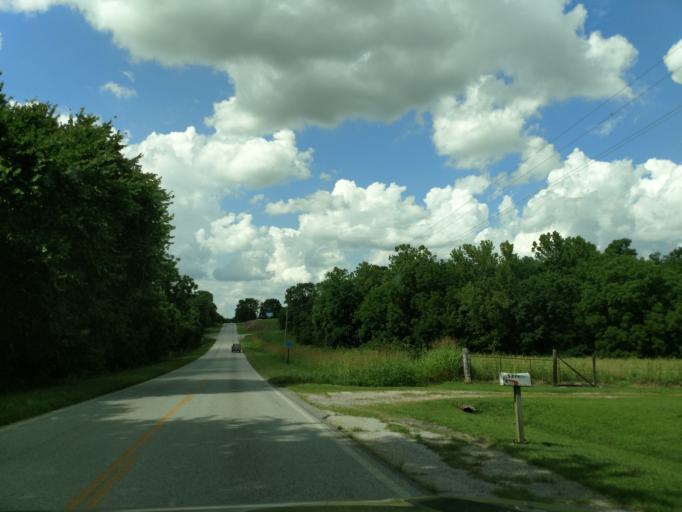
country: US
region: Arkansas
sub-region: Carroll County
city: Berryville
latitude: 36.3997
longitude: -93.5660
